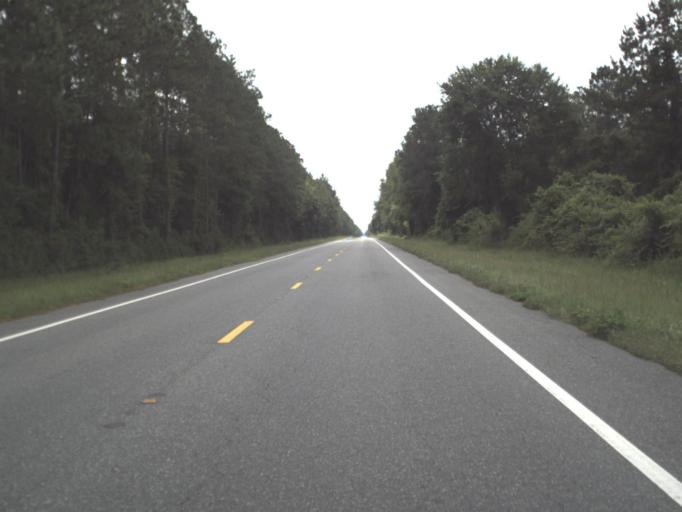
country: US
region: Florida
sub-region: Columbia County
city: Watertown
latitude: 30.1528
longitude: -82.5557
